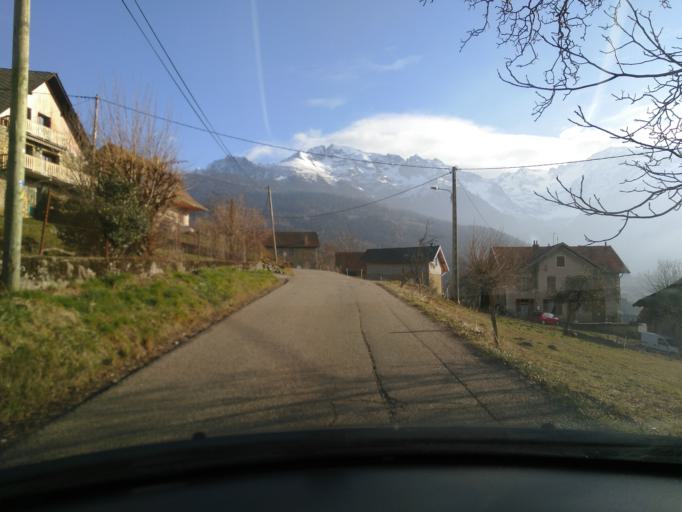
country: FR
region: Rhone-Alpes
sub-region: Departement de l'Isere
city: Froges
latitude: 45.2361
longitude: 5.9322
